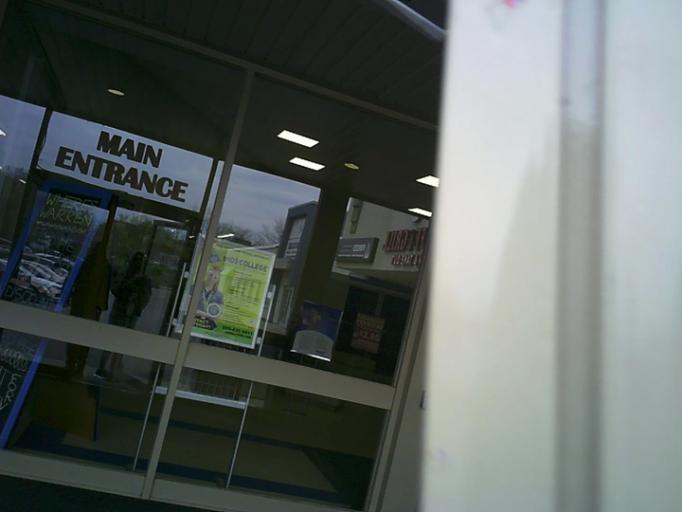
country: CA
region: Ontario
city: Oshawa
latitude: 43.8939
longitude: -78.8678
